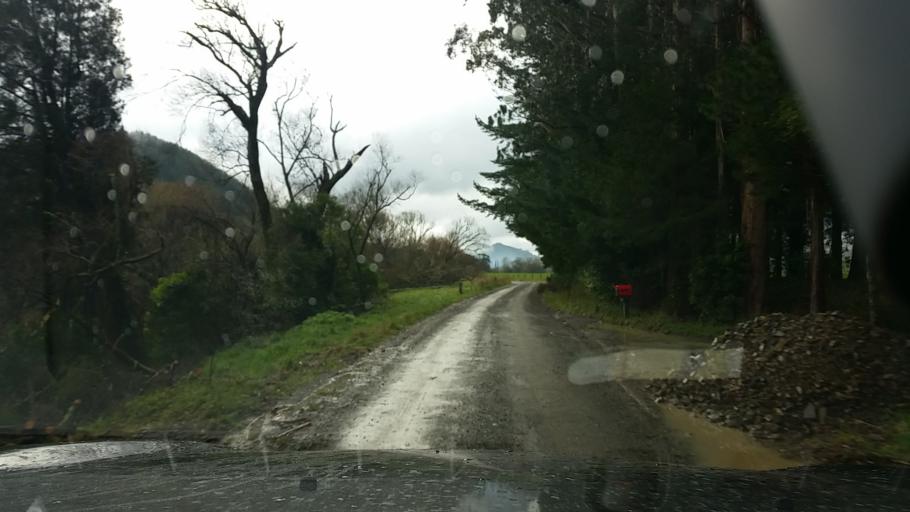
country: NZ
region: Nelson
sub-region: Nelson City
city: Nelson
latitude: -41.2641
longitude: 173.5762
